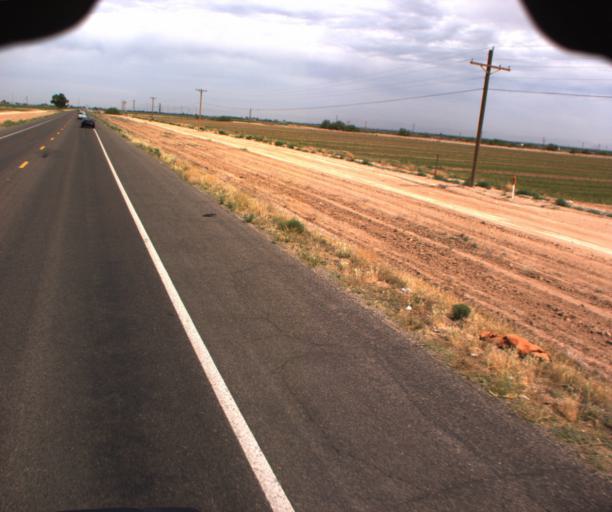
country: US
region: Arizona
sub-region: Pinal County
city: Eloy
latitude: 32.8463
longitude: -111.5152
